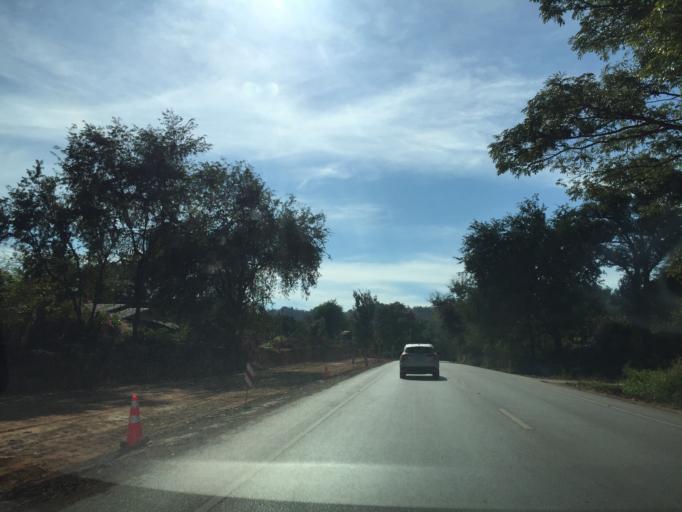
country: TH
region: Loei
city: Wang Saphung
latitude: 17.2894
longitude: 101.8415
